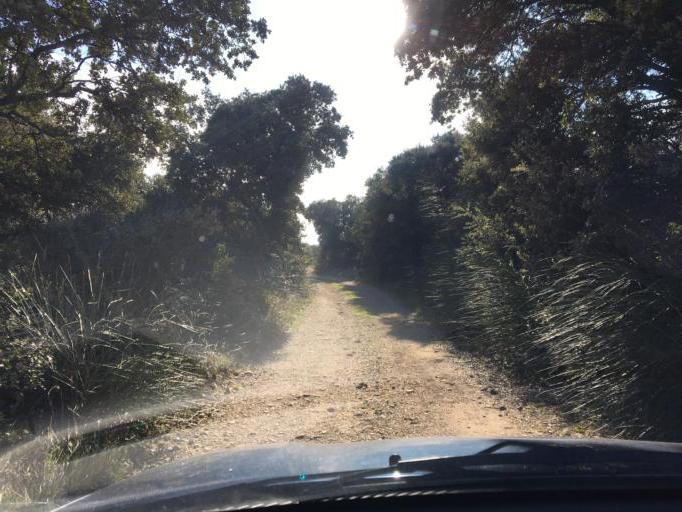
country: FR
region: Provence-Alpes-Cote d'Azur
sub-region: Departement du Vaucluse
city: Camaret-sur-Aigues
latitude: 44.1539
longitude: 4.8963
